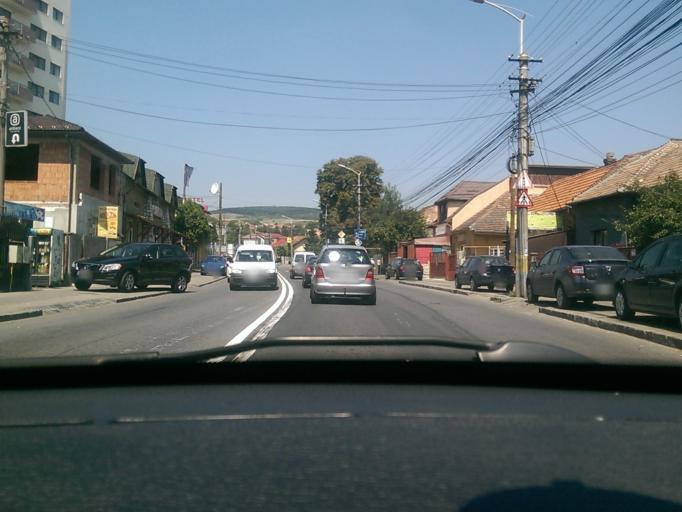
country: RO
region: Cluj
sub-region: Municipiul Cluj-Napoca
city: Cluj-Napoca
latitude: 46.7871
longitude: 23.5809
